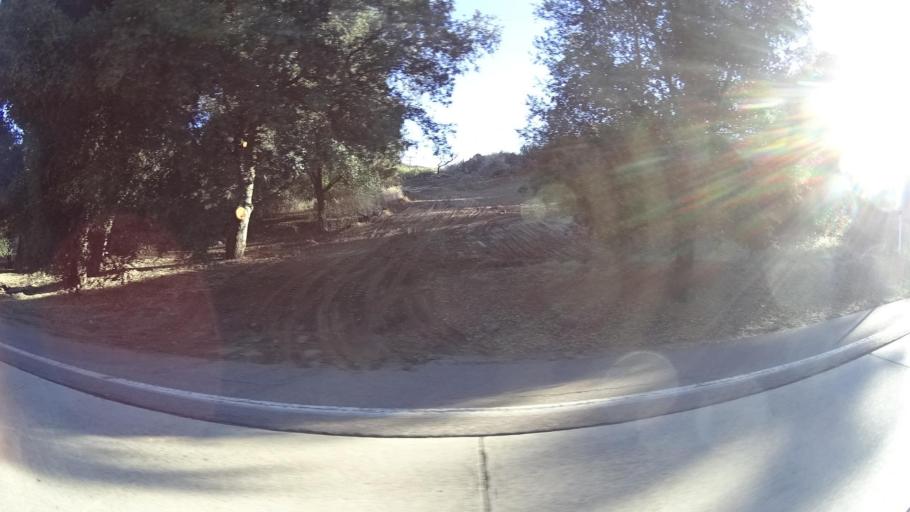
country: US
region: California
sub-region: San Diego County
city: Pine Valley
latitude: 32.8516
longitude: -116.5641
